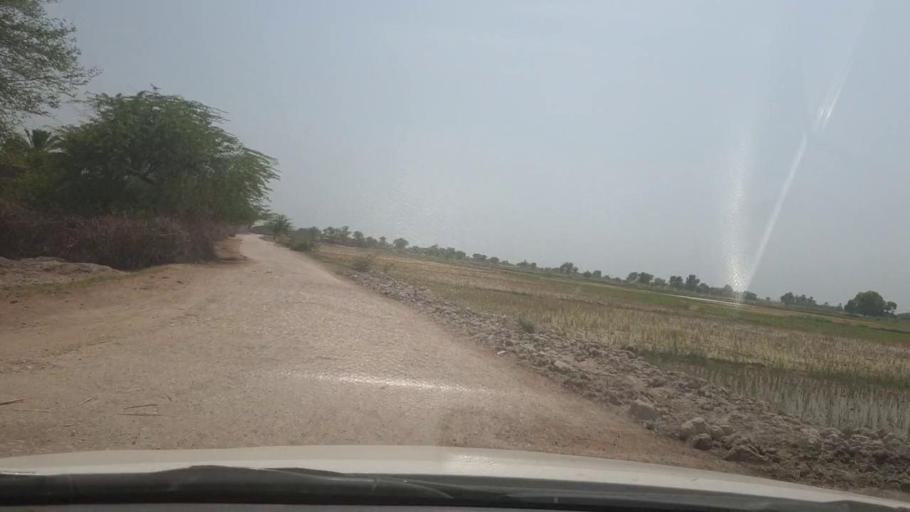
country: PK
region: Sindh
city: Shikarpur
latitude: 27.9992
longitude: 68.5897
